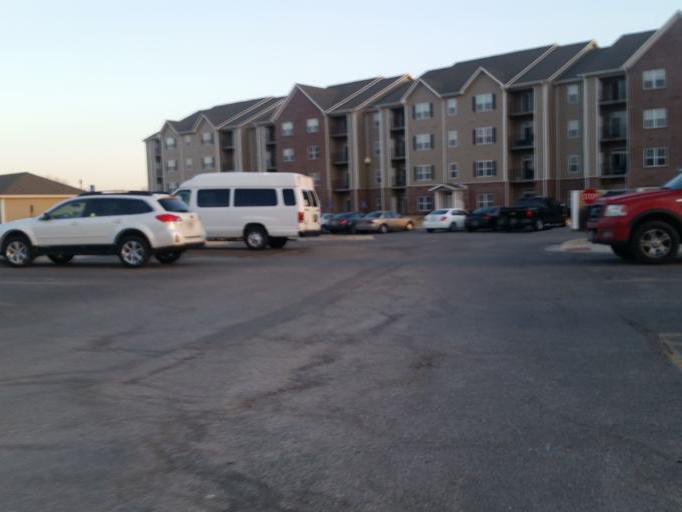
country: US
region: Nebraska
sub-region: Sarpy County
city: Offutt Air Force Base
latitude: 41.1464
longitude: -95.9747
